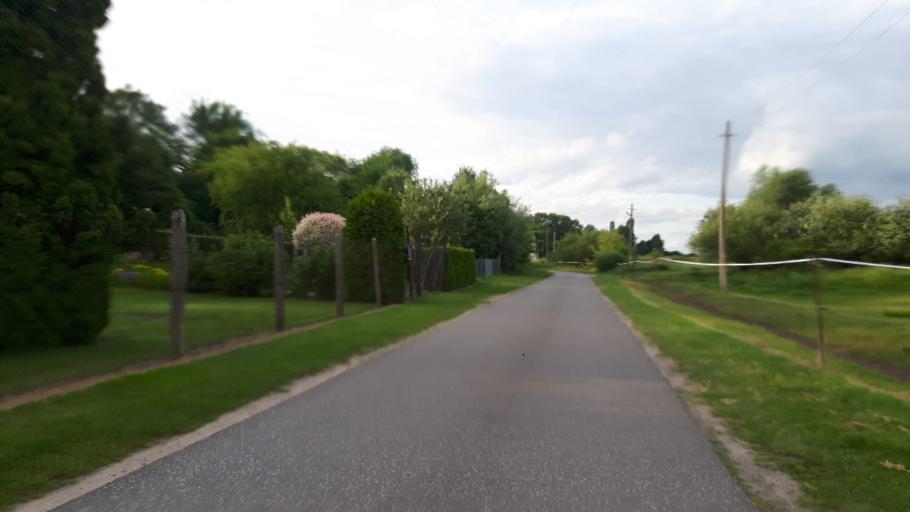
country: DE
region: Brandenburg
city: Gartz
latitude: 53.2088
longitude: 14.3990
